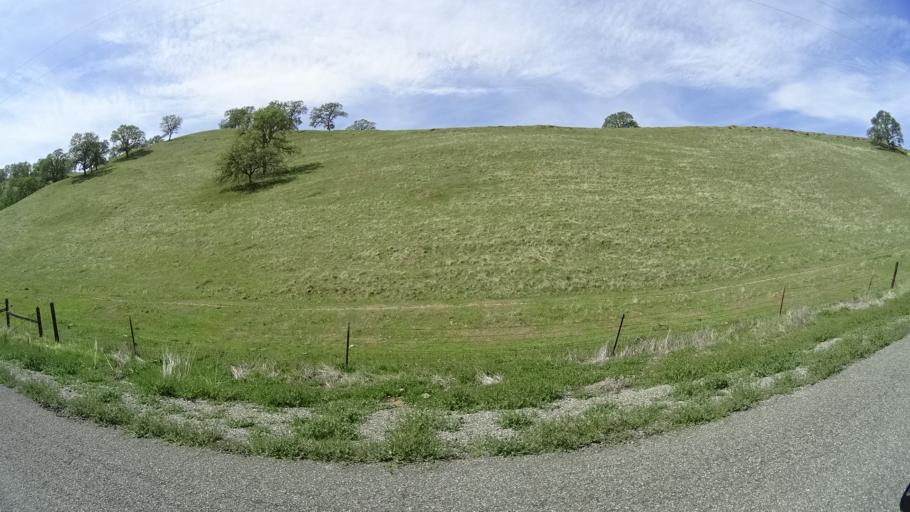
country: US
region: California
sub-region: Glenn County
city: Willows
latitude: 39.5713
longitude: -122.4435
